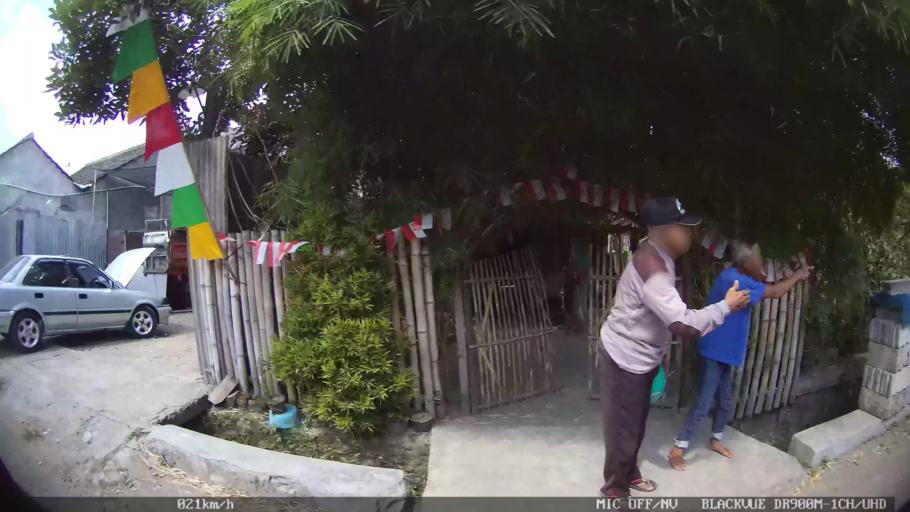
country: ID
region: Daerah Istimewa Yogyakarta
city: Kasihan
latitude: -7.8108
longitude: 110.3370
